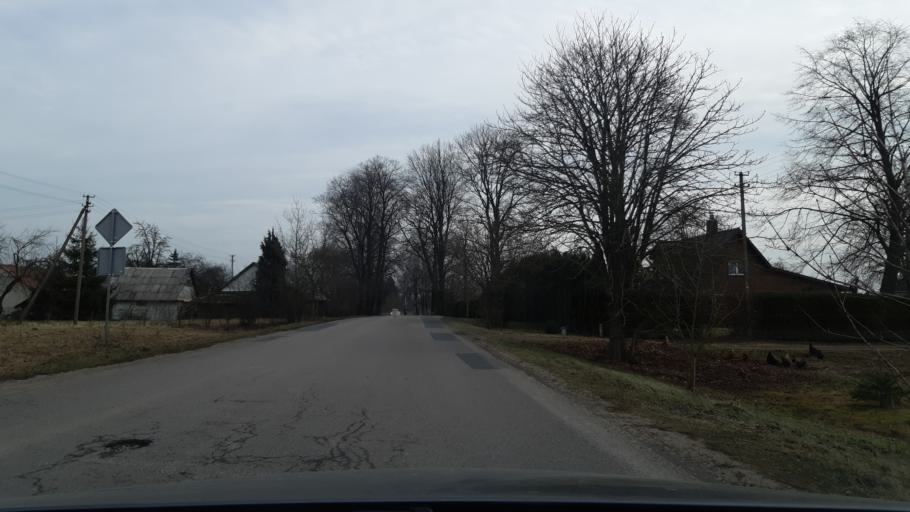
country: LT
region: Marijampoles apskritis
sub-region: Marijampole Municipality
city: Marijampole
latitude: 54.7182
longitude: 23.3241
